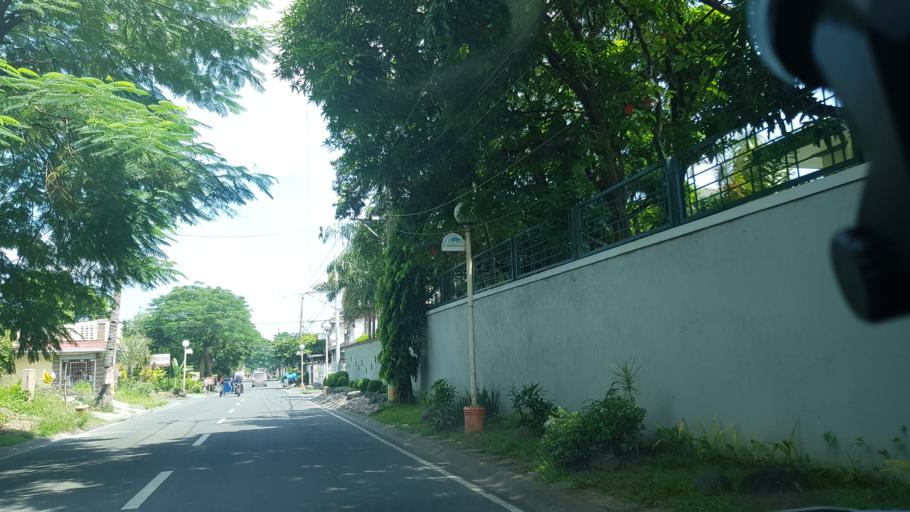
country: PH
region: Calabarzon
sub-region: Province of Rizal
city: Las Pinas
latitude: 14.4291
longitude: 120.9945
